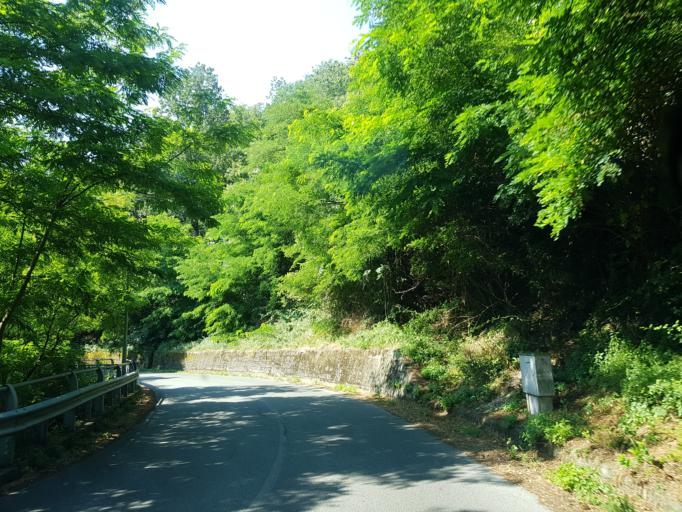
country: IT
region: Liguria
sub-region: Provincia di Genova
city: Manesseno
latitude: 44.4876
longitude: 8.9111
